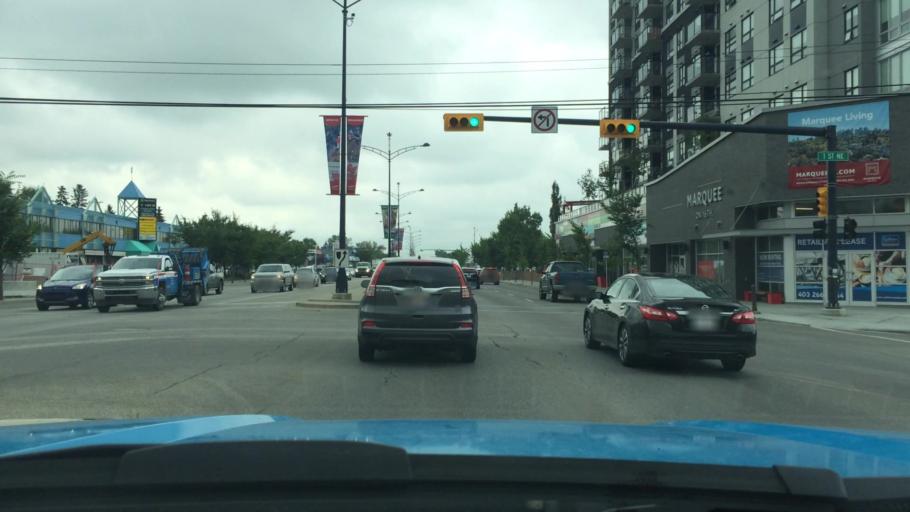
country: CA
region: Alberta
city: Calgary
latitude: 51.0668
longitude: -114.0602
